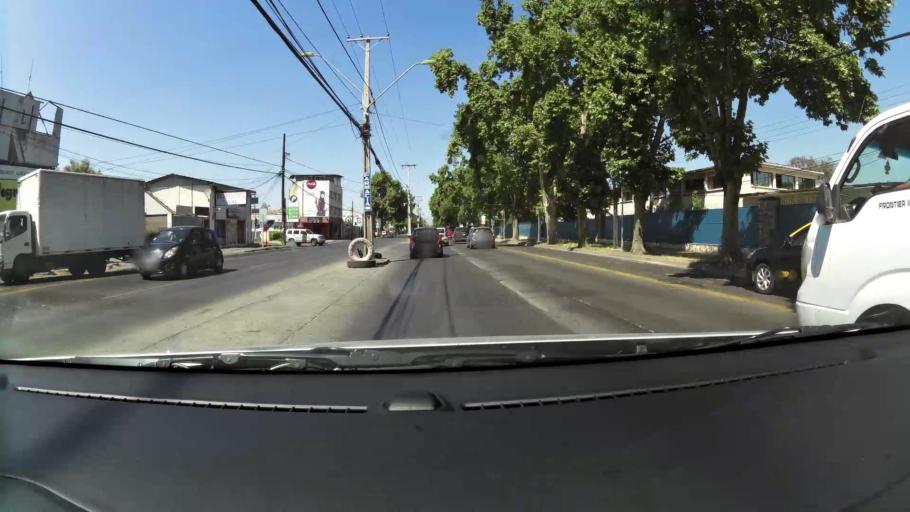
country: CL
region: Santiago Metropolitan
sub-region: Provincia de Maipo
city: San Bernardo
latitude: -33.5578
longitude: -70.6779
